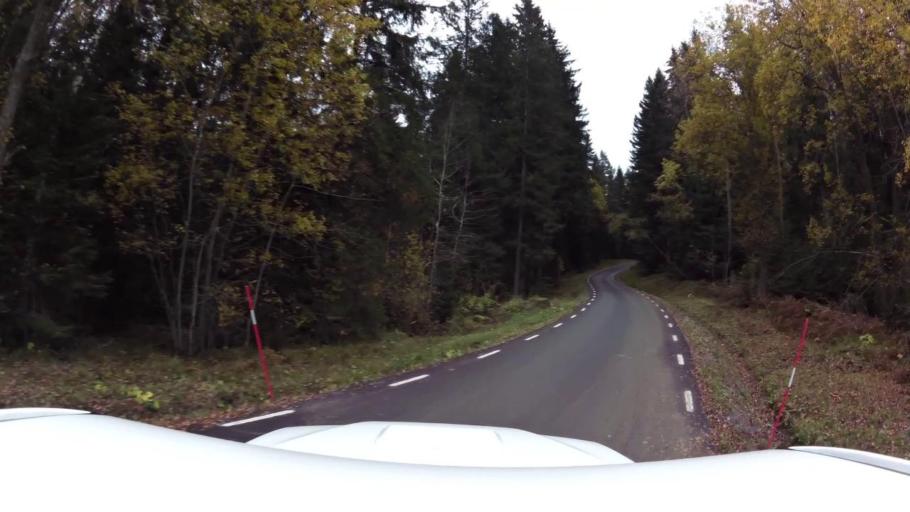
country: SE
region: OEstergoetland
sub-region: Linkopings Kommun
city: Ljungsbro
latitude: 58.5802
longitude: 15.4630
